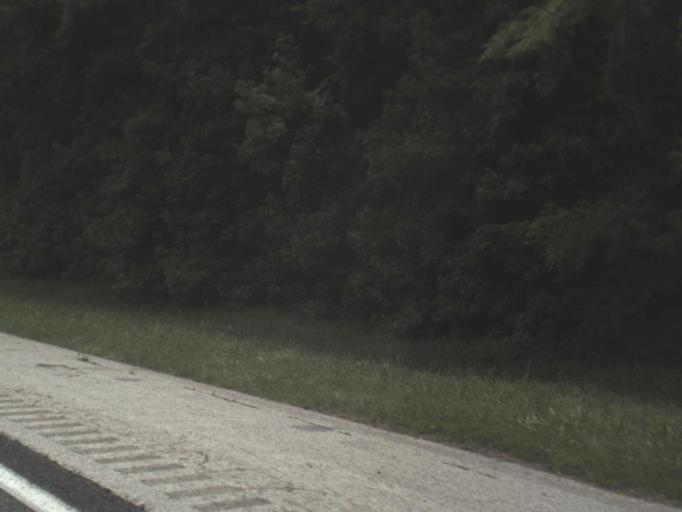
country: US
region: Florida
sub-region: Alachua County
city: High Springs
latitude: 29.8800
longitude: -82.5437
